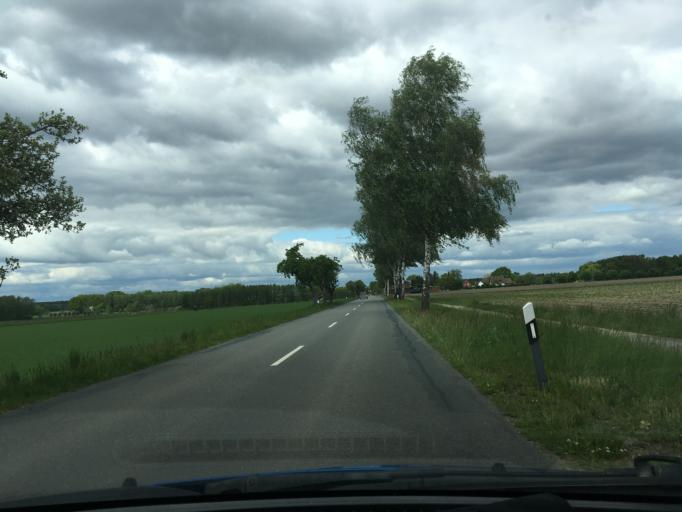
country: DE
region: Lower Saxony
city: Suderburg
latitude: 52.9148
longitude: 10.4194
